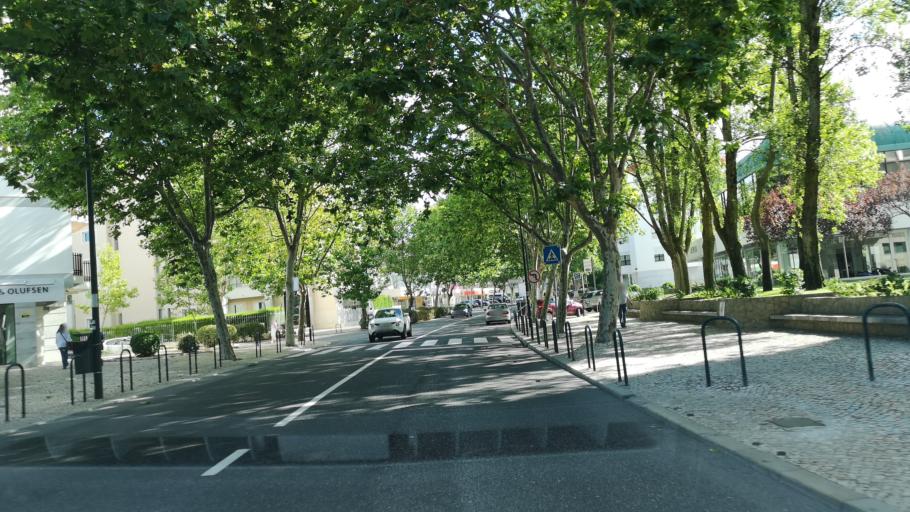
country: PT
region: Lisbon
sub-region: Cascais
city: Cascais
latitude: 38.6971
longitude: -9.4297
